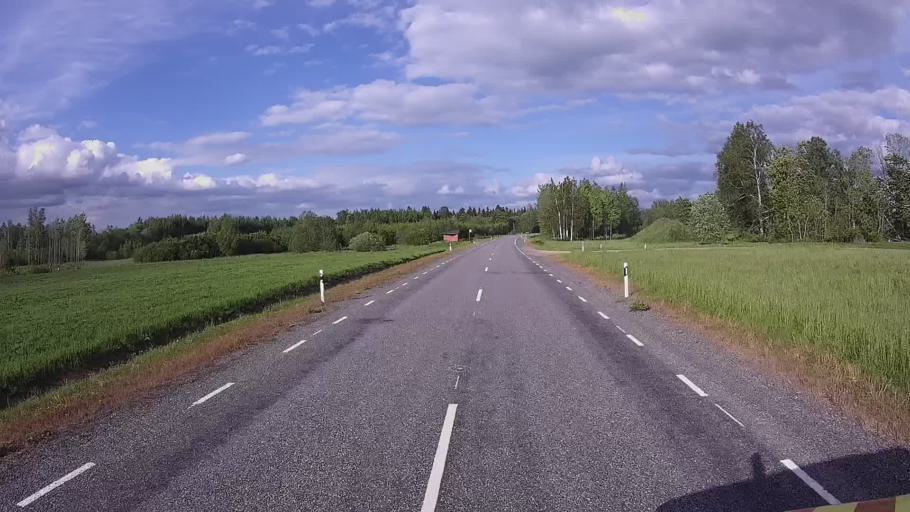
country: EE
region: Jogevamaa
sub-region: Mustvee linn
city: Mustvee
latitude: 59.0250
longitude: 26.9812
